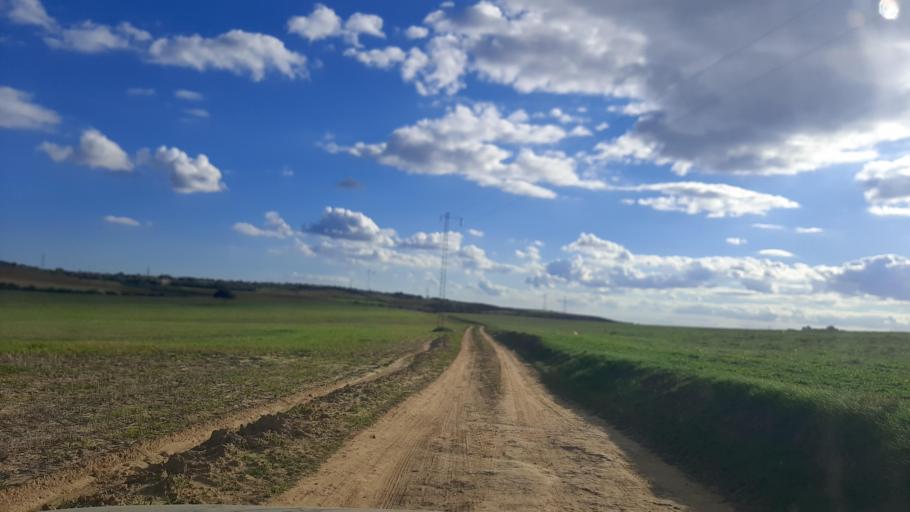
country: TN
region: Nabul
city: Bu `Urqub
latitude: 36.4501
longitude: 10.5011
